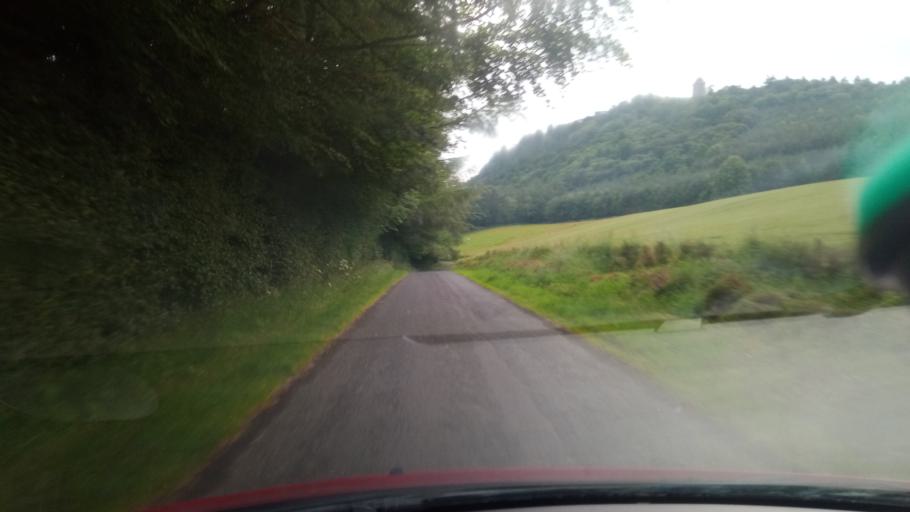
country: GB
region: Scotland
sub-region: The Scottish Borders
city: Saint Boswells
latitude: 55.4808
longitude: -2.6526
